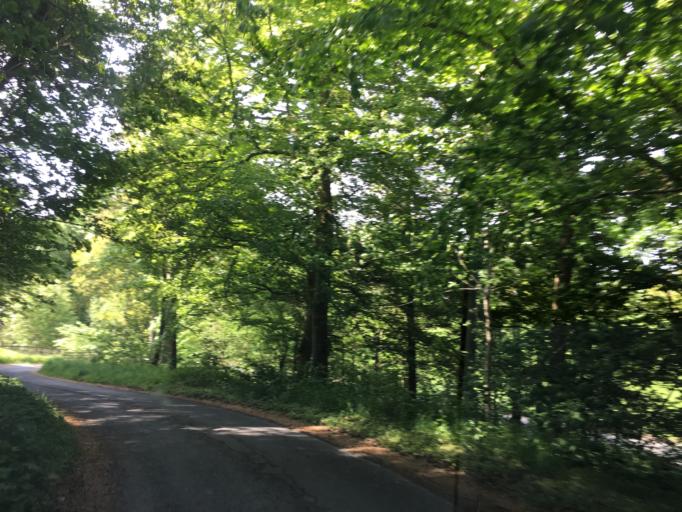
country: GB
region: Scotland
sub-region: South Lanarkshire
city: Biggar
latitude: 55.6181
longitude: -3.4121
